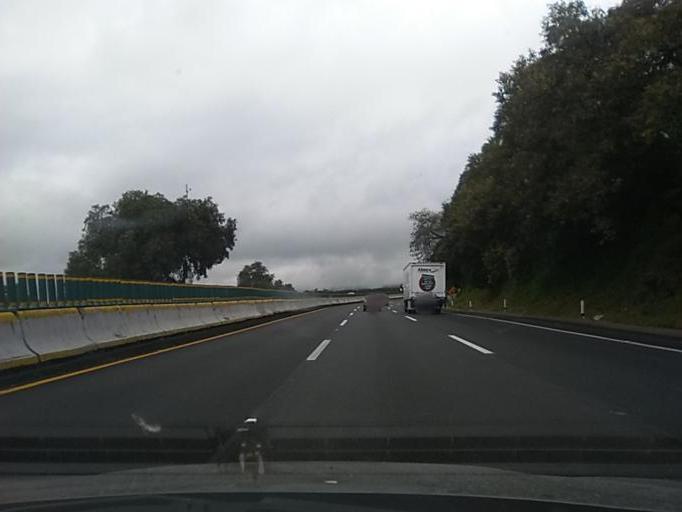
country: MX
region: Mexico City
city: Xochimilco
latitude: 19.2259
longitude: -99.1296
